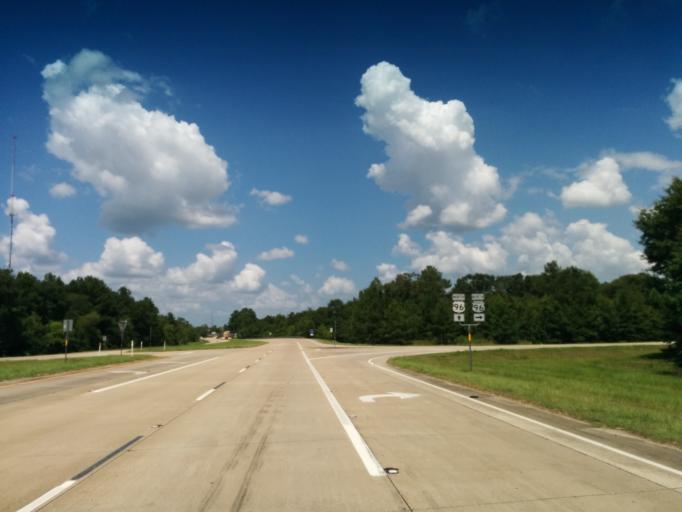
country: US
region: Texas
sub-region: Jasper County
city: Buna
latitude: 30.4269
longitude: -93.9827
